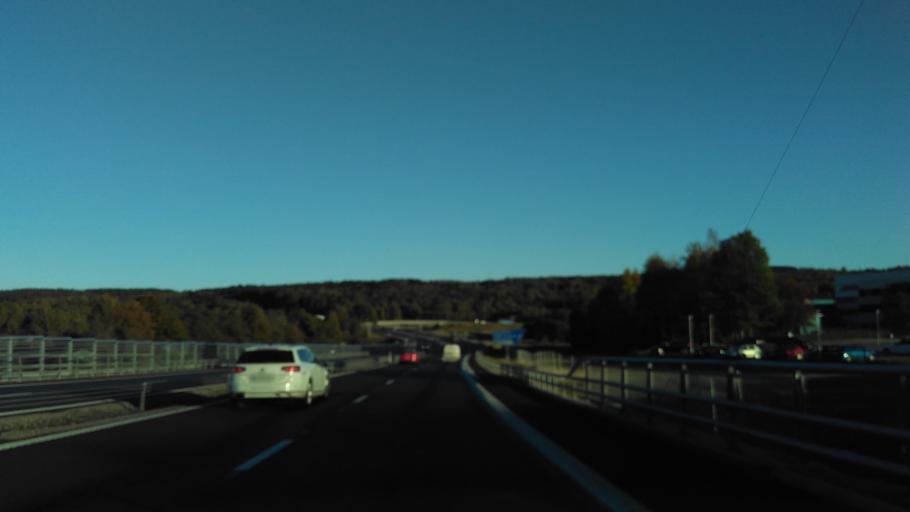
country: SE
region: Vaestra Goetaland
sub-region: Ulricehamns Kommun
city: Ulricehamn
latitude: 57.8112
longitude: 13.4116
